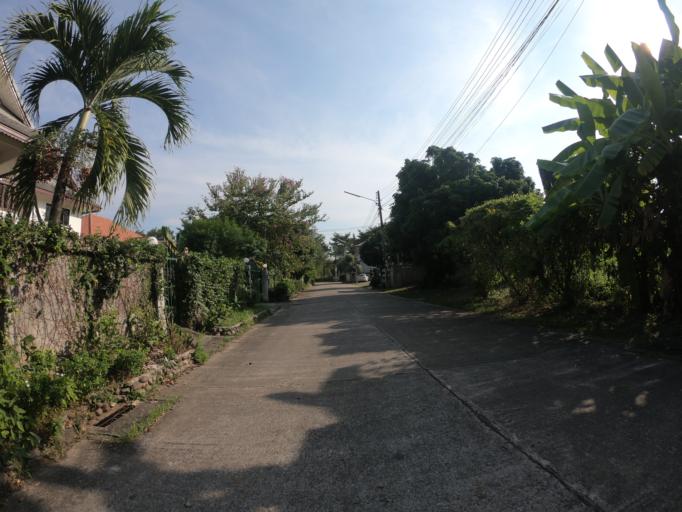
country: TH
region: Chiang Mai
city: Chiang Mai
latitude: 18.8220
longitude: 98.9975
